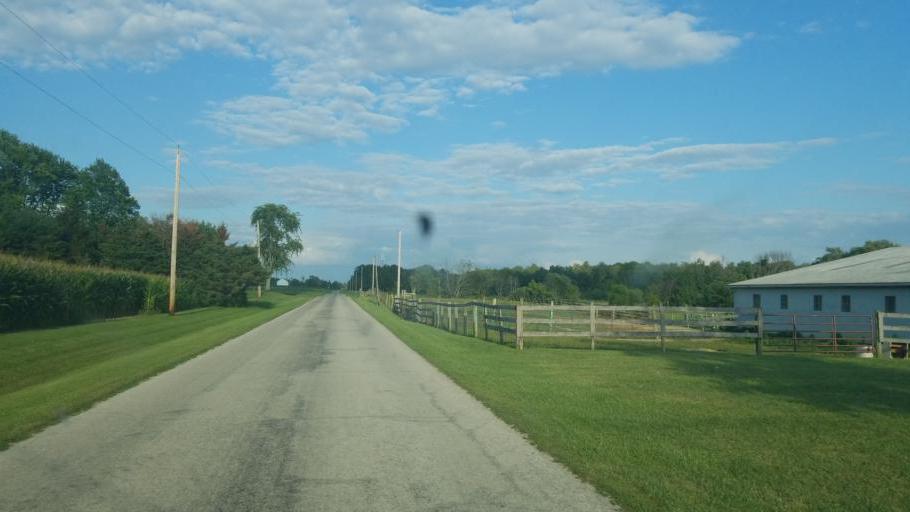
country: US
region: Ohio
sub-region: Seneca County
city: Tiffin
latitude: 41.1098
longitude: -83.0417
